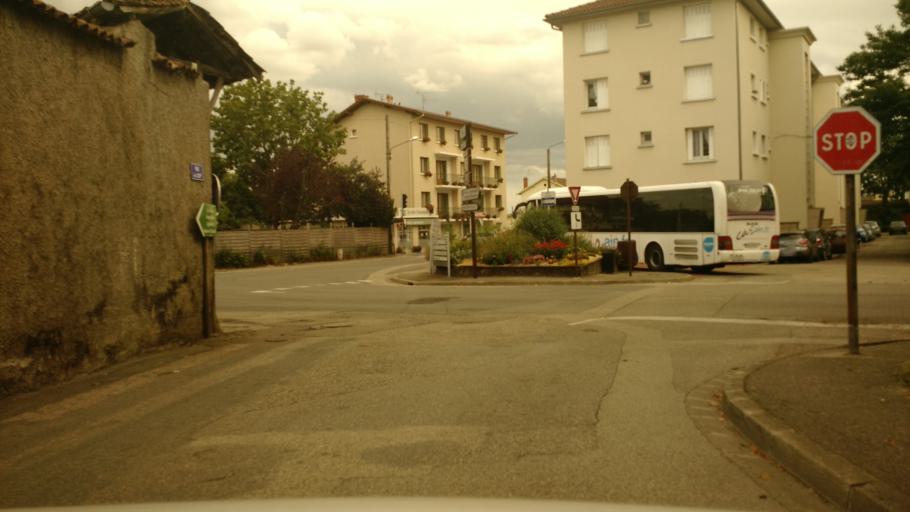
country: FR
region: Rhone-Alpes
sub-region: Departement de l'Ain
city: Montluel
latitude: 45.8516
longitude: 5.0620
